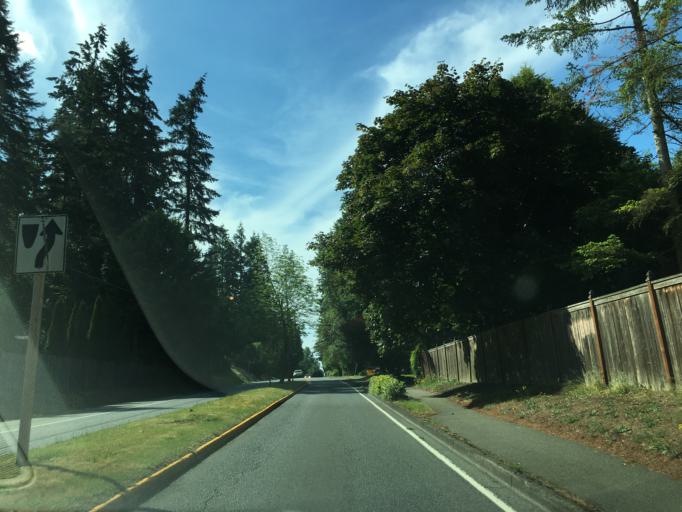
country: US
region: Washington
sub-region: King County
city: Lake Forest Park
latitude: 47.7658
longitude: -122.2964
